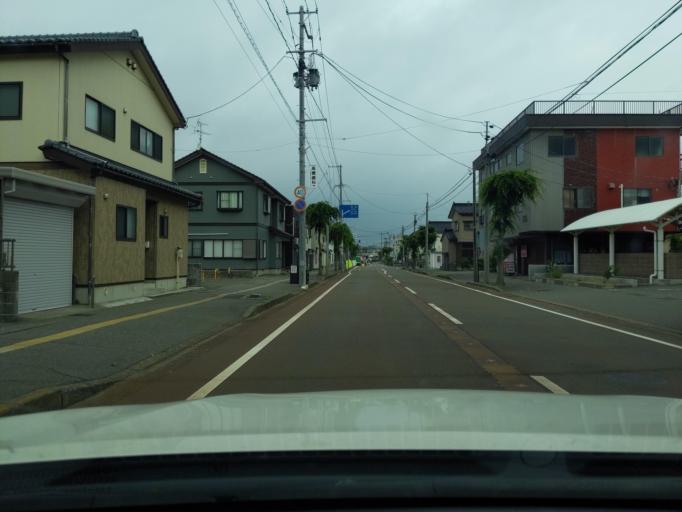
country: JP
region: Niigata
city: Kashiwazaki
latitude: 37.3721
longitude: 138.5577
